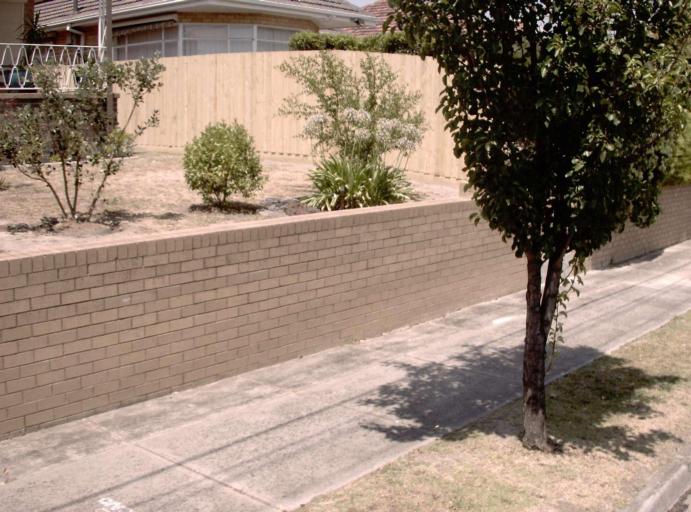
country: AU
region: Victoria
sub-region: Manningham
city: Bulleen
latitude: -37.7717
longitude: 145.0976
